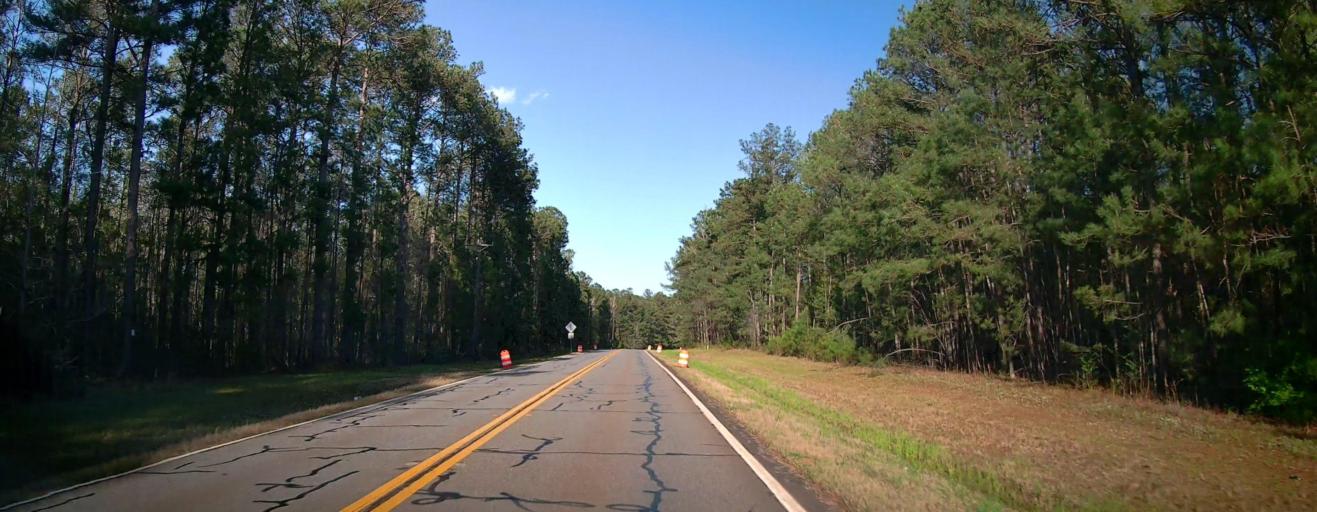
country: US
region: Georgia
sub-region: Baldwin County
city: Milledgeville
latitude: 33.1275
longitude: -83.3107
